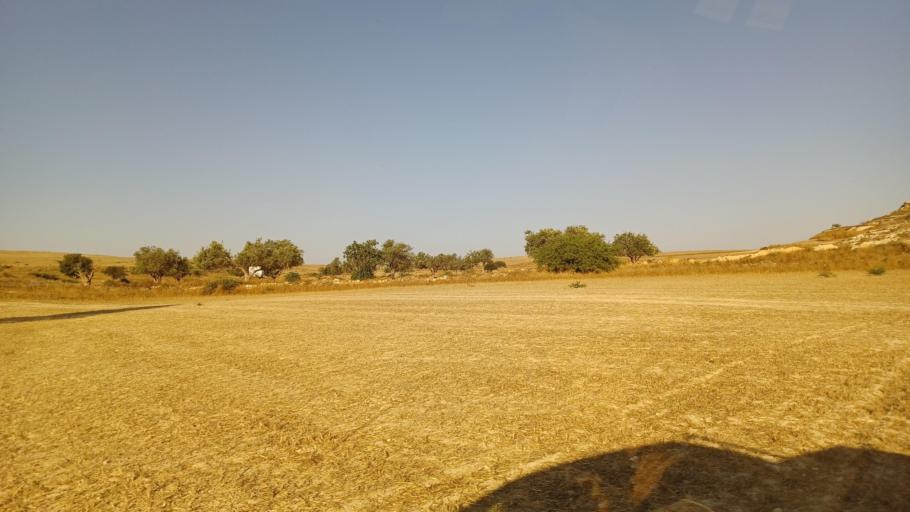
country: CY
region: Larnaka
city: Athienou
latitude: 35.0422
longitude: 33.5157
